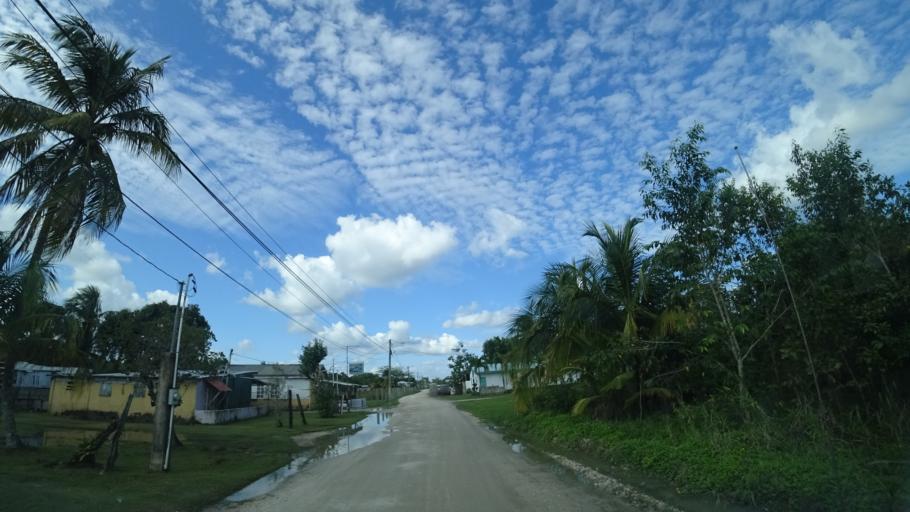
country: BZ
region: Belize
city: Belize City
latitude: 17.5662
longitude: -88.4086
